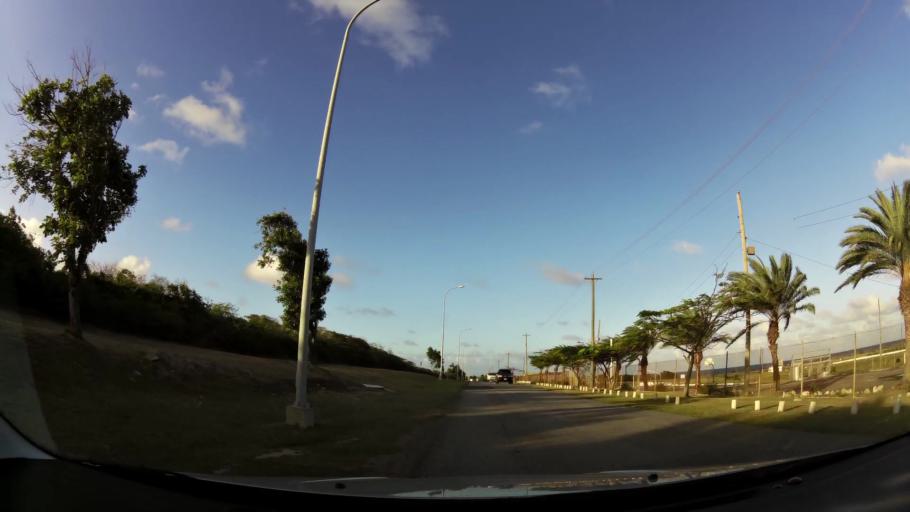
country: AG
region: Saint George
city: Piggotts
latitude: 17.1582
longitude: -61.7982
